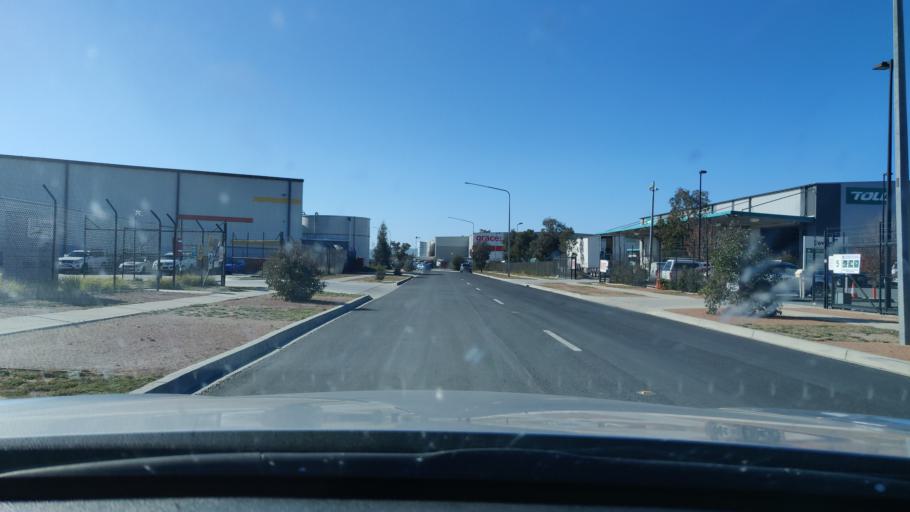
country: AU
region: Australian Capital Territory
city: Macarthur
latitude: -35.3992
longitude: 149.1628
